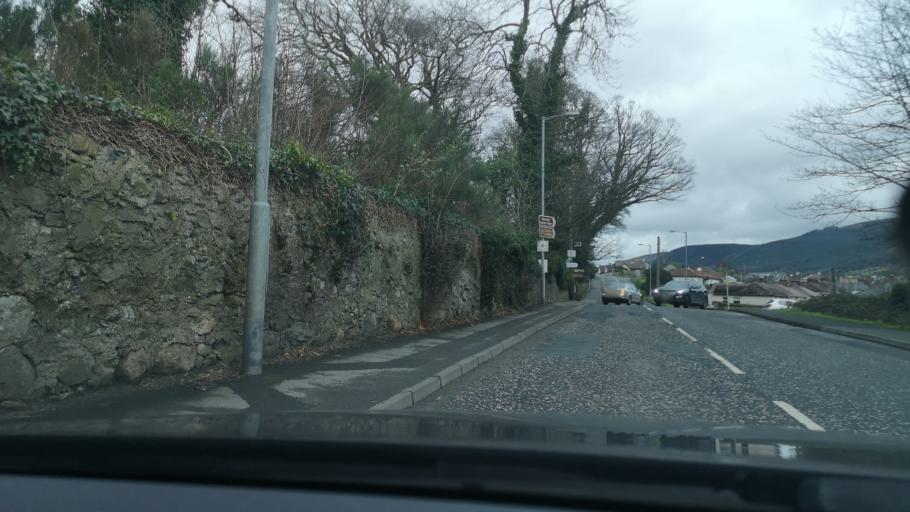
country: GB
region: Northern Ireland
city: Rostrevor
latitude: 54.1046
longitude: -6.1919
